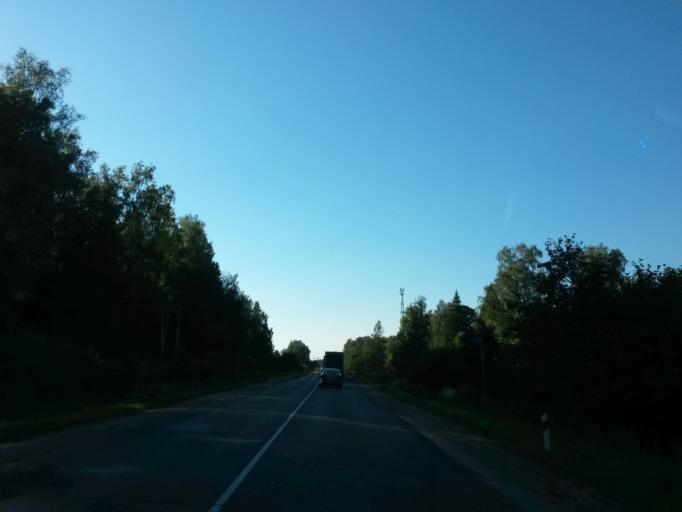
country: RU
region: Ivanovo
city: Novo-Talitsy
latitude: 57.0576
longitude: 40.7258
